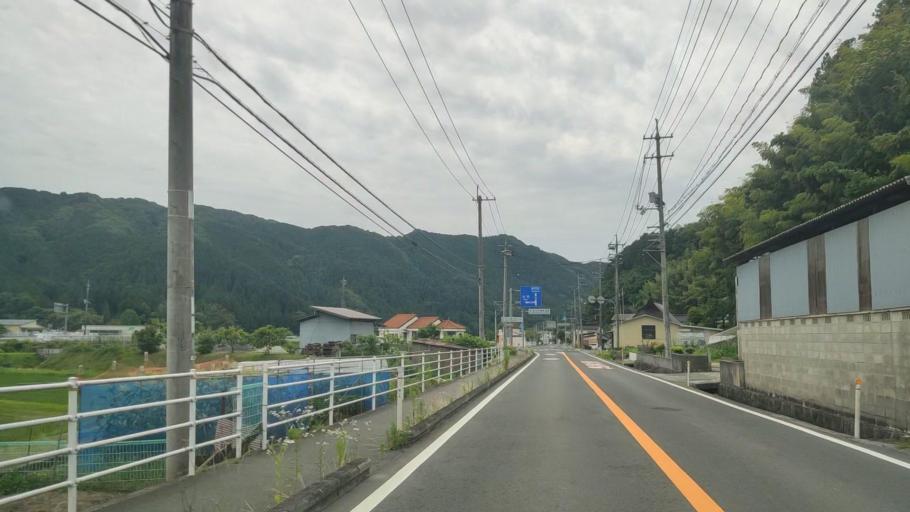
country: JP
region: Hyogo
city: Yamazakicho-nakabirose
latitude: 35.0987
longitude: 134.3235
